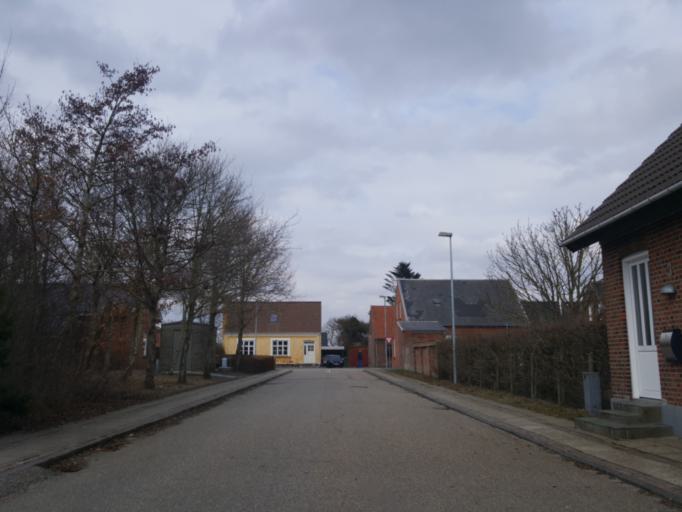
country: DK
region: Central Jutland
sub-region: Holstebro Kommune
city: Ulfborg
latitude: 56.3426
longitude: 8.3413
